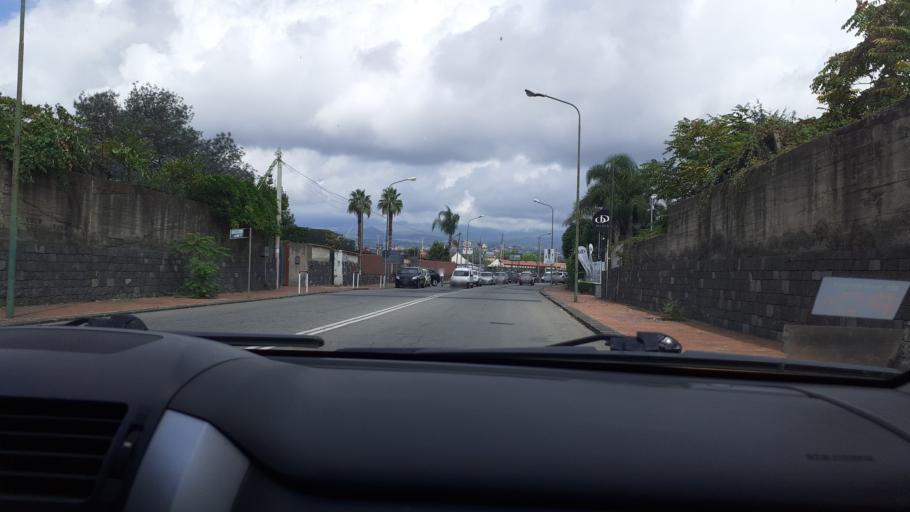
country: IT
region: Sicily
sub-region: Catania
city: San Gregorio di Catania
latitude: 37.5649
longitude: 15.1061
